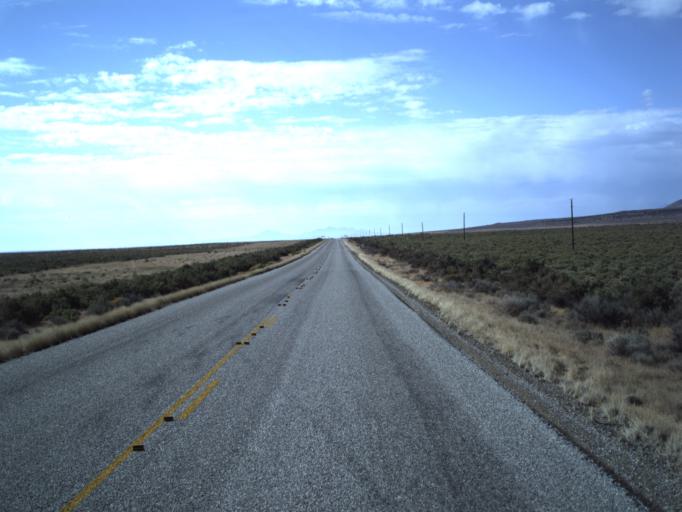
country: US
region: Utah
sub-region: Tooele County
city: Wendover
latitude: 41.5589
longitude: -113.5839
